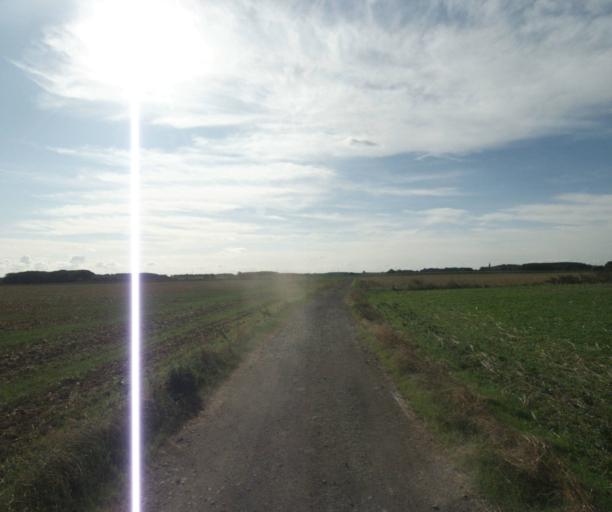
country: FR
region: Nord-Pas-de-Calais
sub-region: Departement du Nord
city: Anstaing
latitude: 50.5965
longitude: 3.1794
